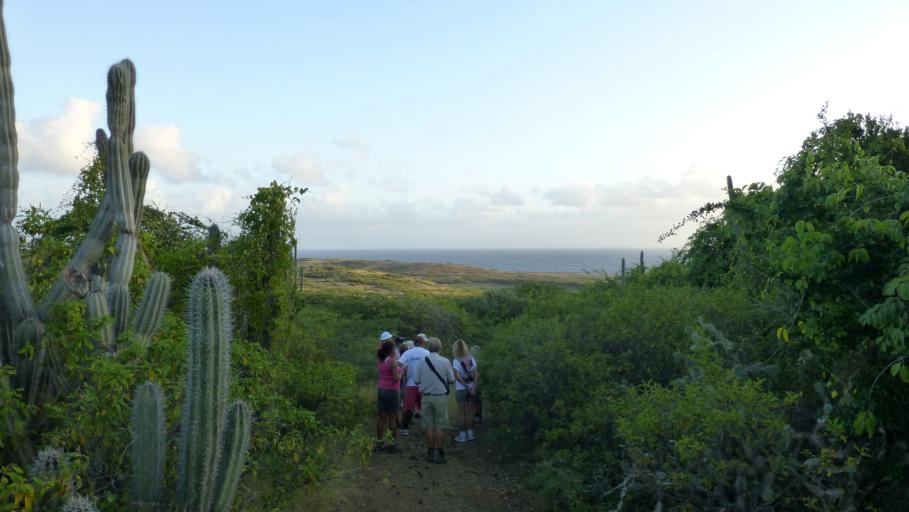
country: CW
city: Dorp Soto
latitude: 12.3737
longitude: -69.1403
